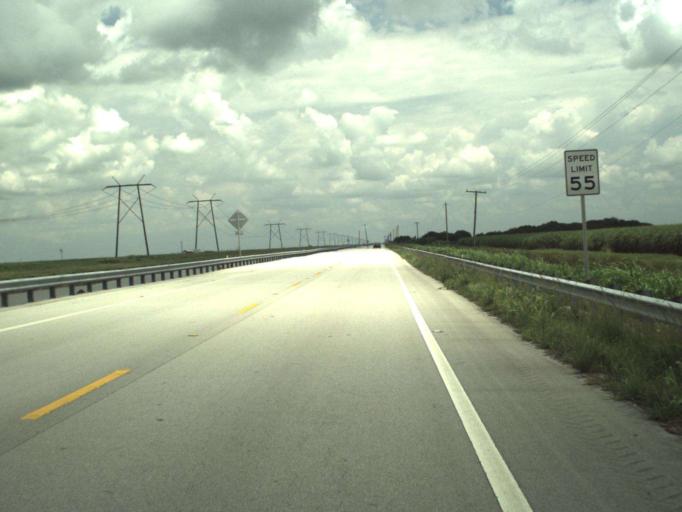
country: US
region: Florida
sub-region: Palm Beach County
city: Pahokee
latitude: 26.7597
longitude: -80.4933
